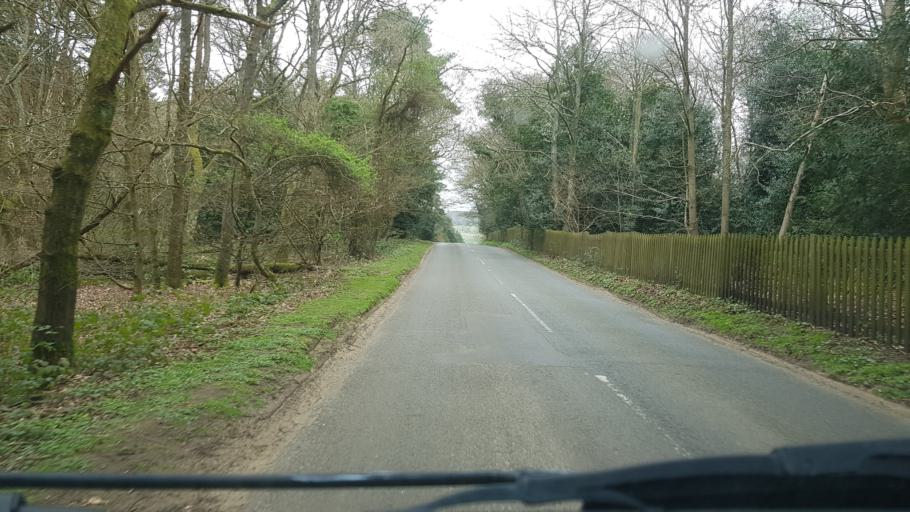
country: GB
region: England
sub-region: Surrey
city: Chilworth
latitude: 51.2136
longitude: -0.4845
